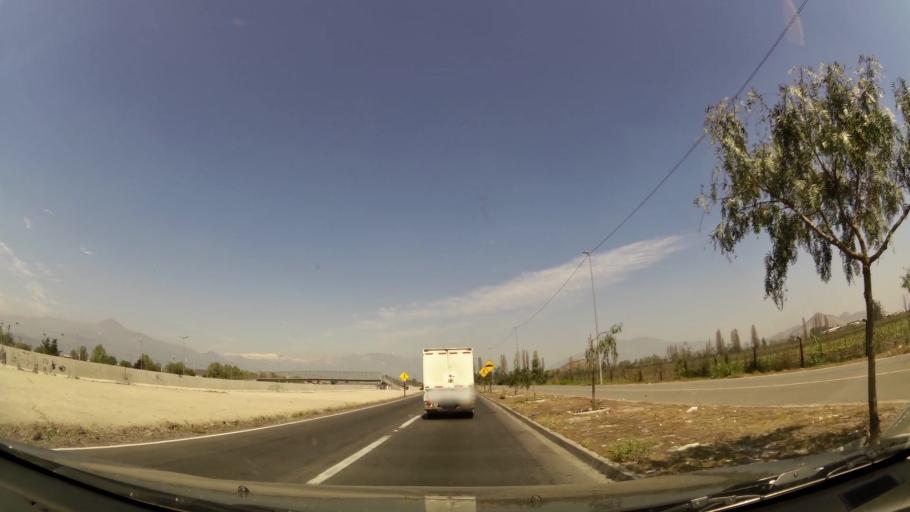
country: CL
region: Santiago Metropolitan
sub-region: Provincia de Cordillera
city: Puente Alto
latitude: -33.6091
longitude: -70.6040
